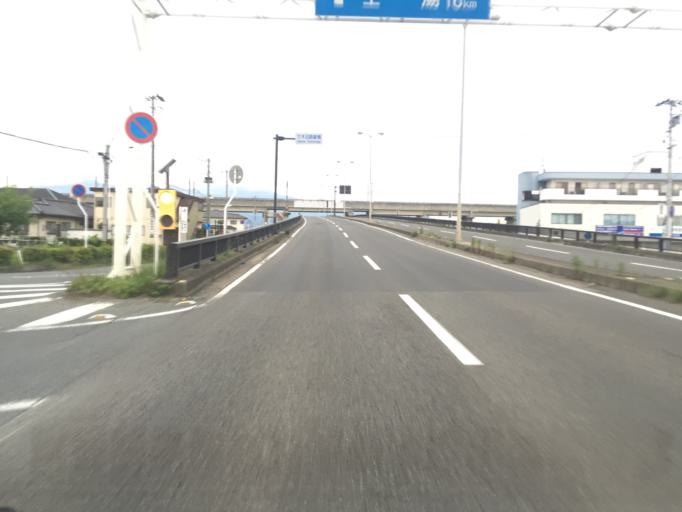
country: JP
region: Fukushima
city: Fukushima-shi
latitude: 37.7390
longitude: 140.4614
